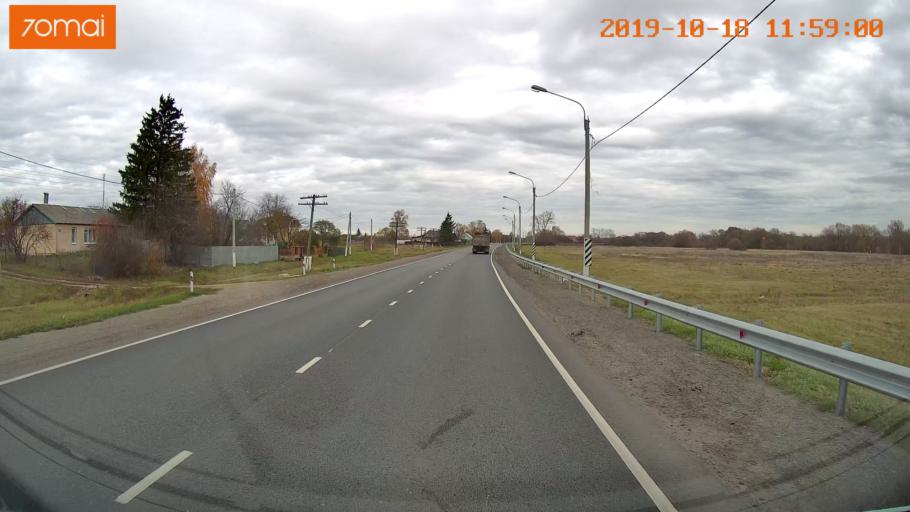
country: RU
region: Rjazan
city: Zakharovo
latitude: 54.2775
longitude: 39.1716
